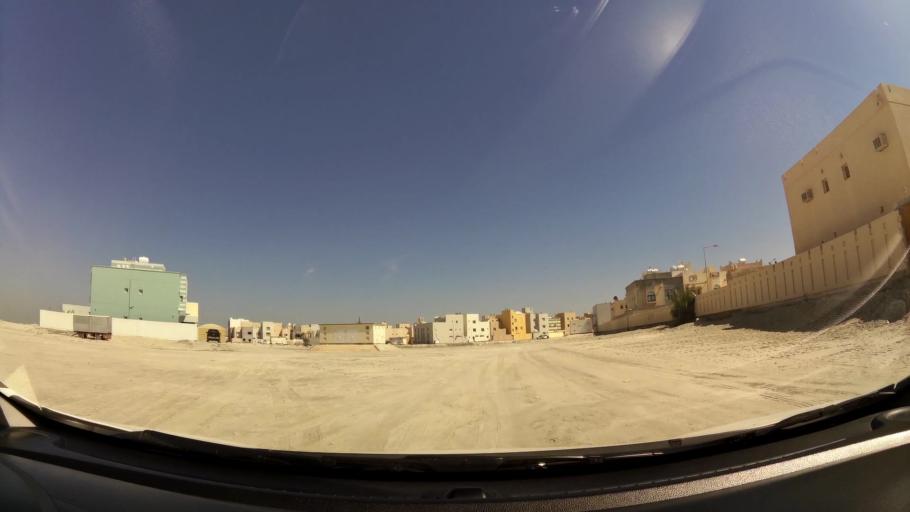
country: BH
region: Muharraq
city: Al Muharraq
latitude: 26.2719
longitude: 50.5951
